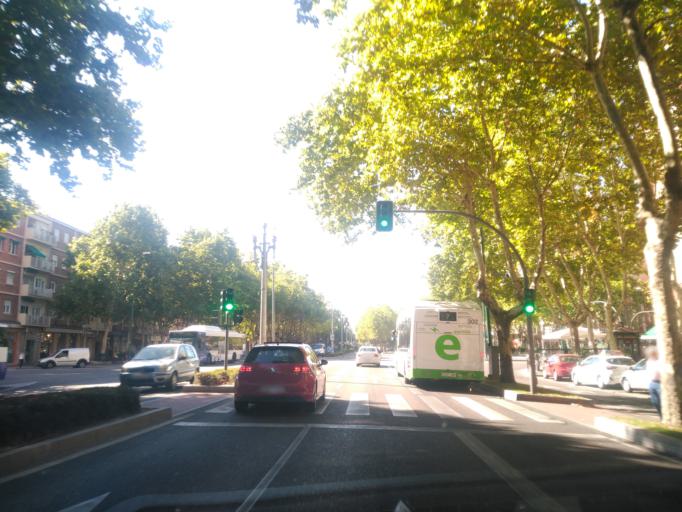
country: ES
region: Castille and Leon
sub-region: Provincia de Valladolid
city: Valladolid
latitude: 41.6413
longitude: -4.7376
